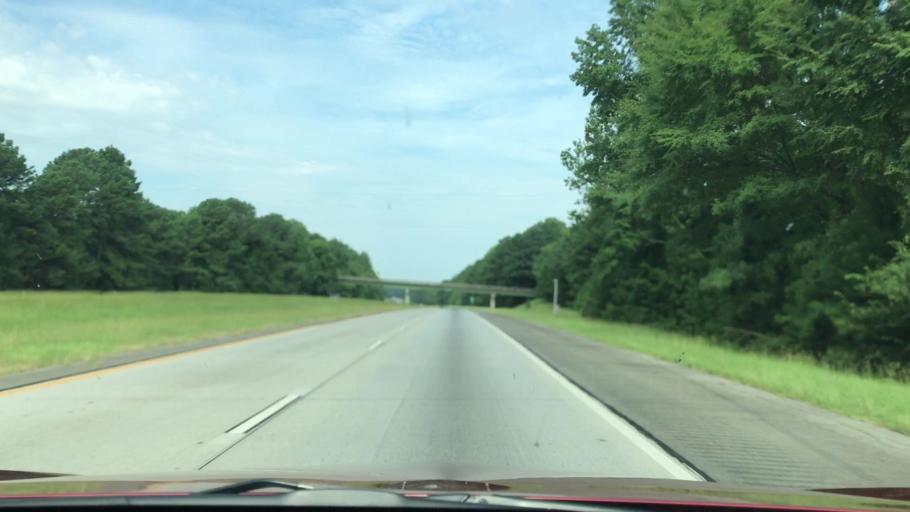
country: US
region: Georgia
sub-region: Warren County
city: Firing Range
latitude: 33.5043
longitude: -82.7461
